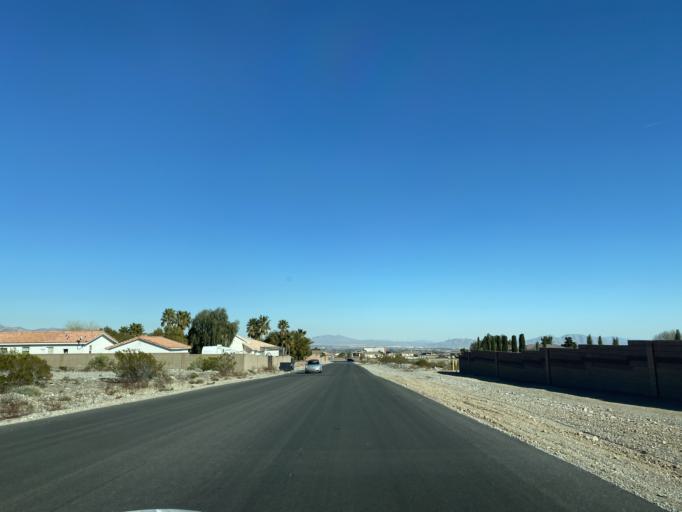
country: US
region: Nevada
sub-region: Clark County
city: Summerlin South
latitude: 36.2883
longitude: -115.3100
